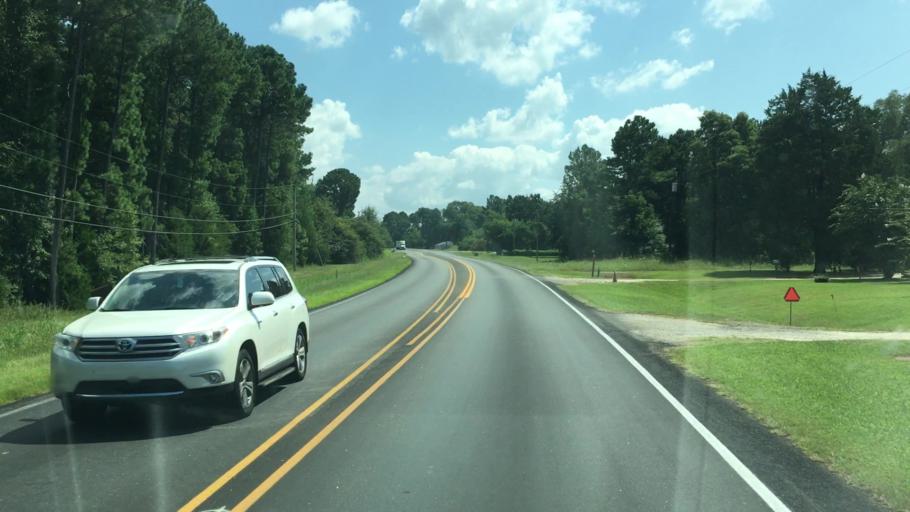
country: US
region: Georgia
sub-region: Morgan County
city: Madison
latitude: 33.6195
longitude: -83.4512
